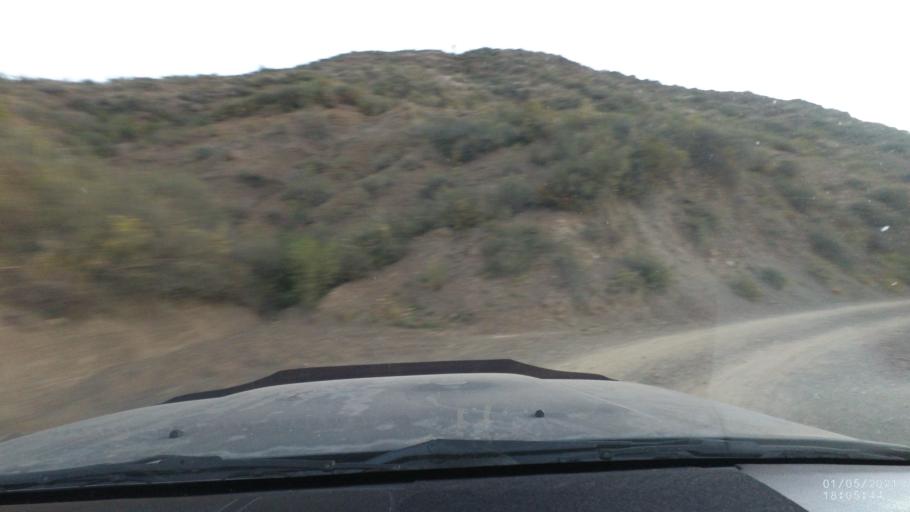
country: BO
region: Cochabamba
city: Capinota
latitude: -17.6885
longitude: -66.1831
